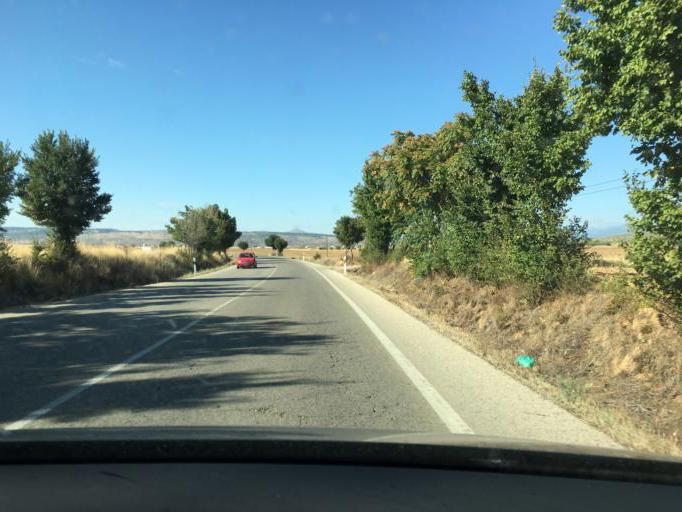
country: ES
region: Madrid
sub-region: Provincia de Madrid
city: Torrelaguna
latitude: 40.8360
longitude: -3.5182
